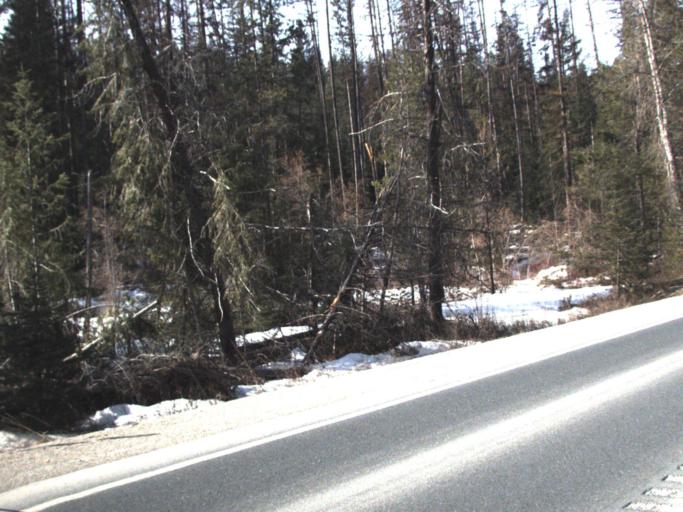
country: US
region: Washington
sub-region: Stevens County
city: Chewelah
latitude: 48.5301
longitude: -117.6251
